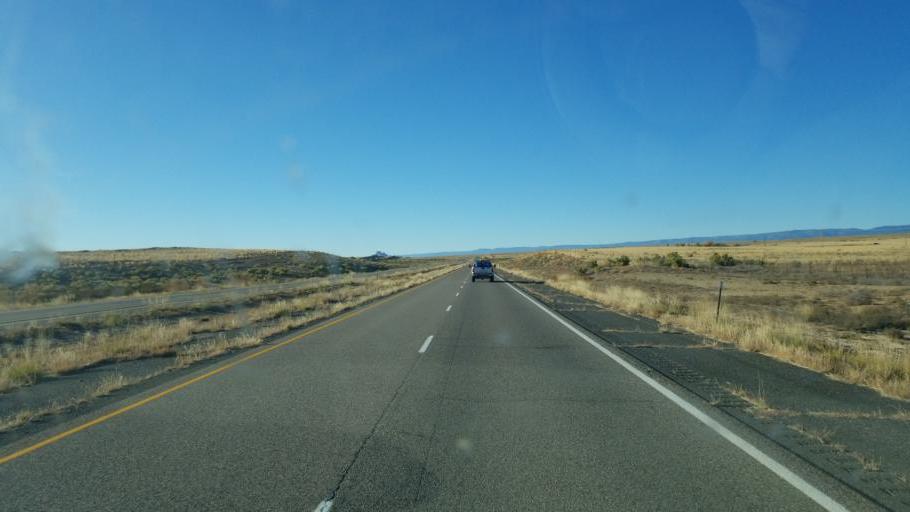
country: US
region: New Mexico
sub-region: San Juan County
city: Shiprock
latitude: 36.5364
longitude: -108.7209
